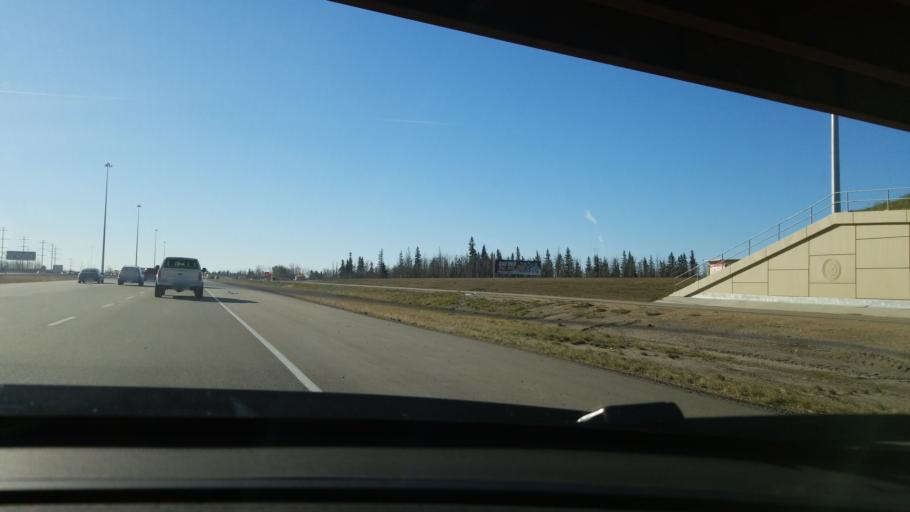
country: CA
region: Alberta
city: Sherwood Park
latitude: 53.5112
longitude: -113.3445
